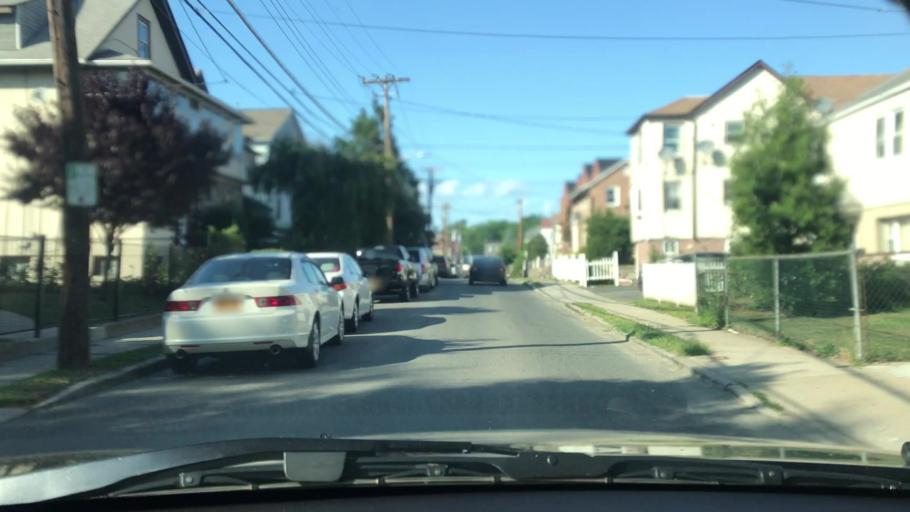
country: US
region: New York
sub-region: Westchester County
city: Mamaroneck
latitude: 40.9520
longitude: -73.7407
